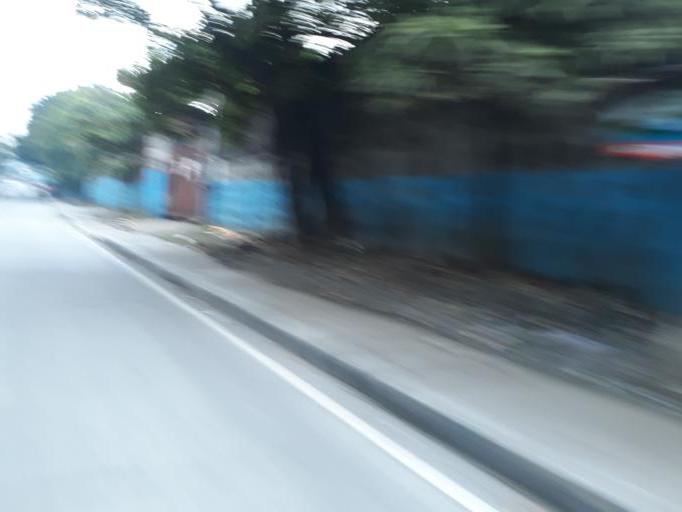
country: PH
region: Calabarzon
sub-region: Province of Rizal
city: Valenzuela
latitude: 14.6970
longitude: 120.9593
